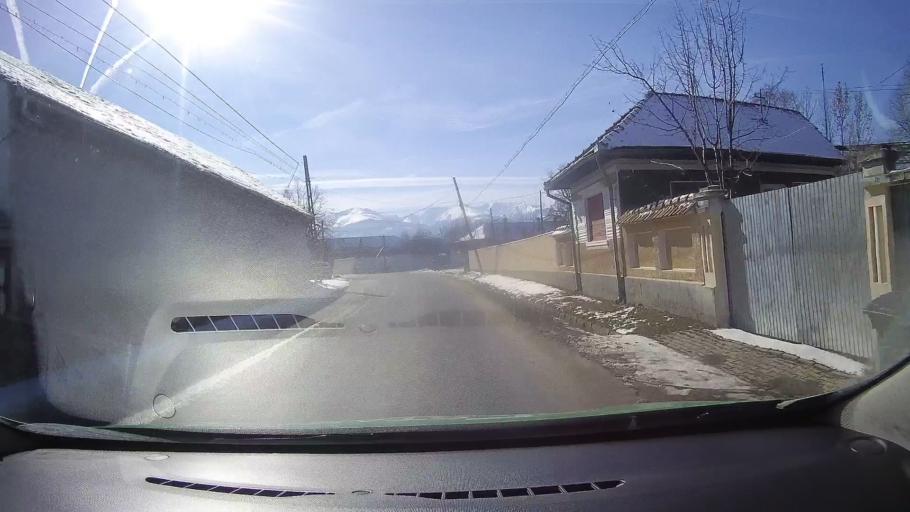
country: RO
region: Brasov
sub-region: Comuna Sambata de Sus
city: Sambata de Sus
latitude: 45.7576
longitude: 24.8305
